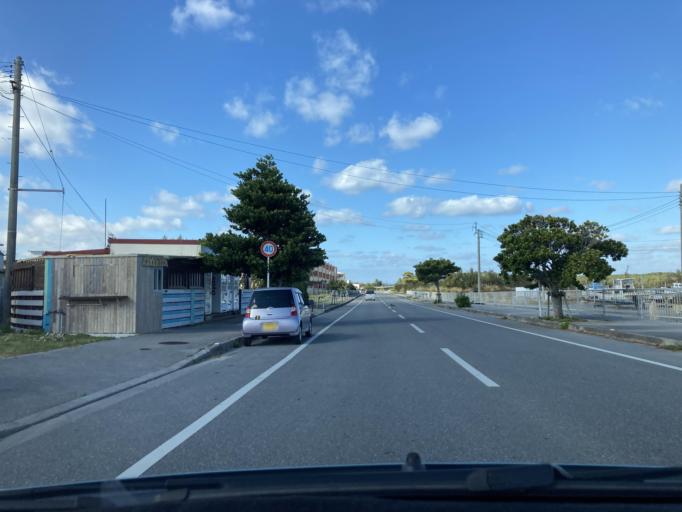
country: JP
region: Okinawa
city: Katsuren-haebaru
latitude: 26.3098
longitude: 127.9202
